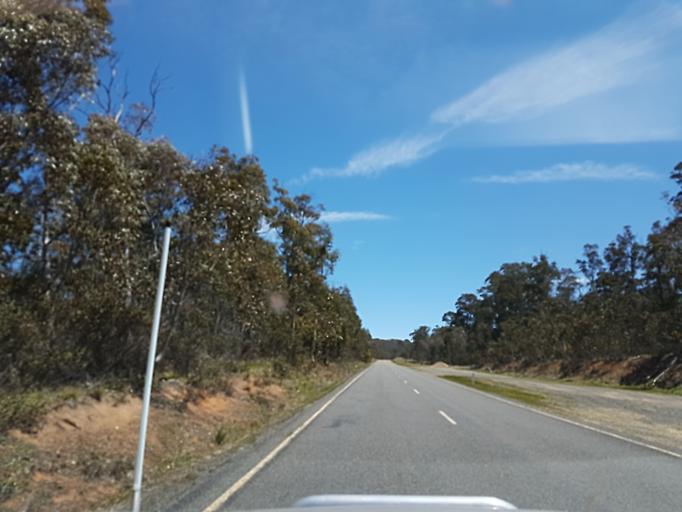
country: AU
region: Victoria
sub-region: Alpine
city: Mount Beauty
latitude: -37.0671
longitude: 147.3418
